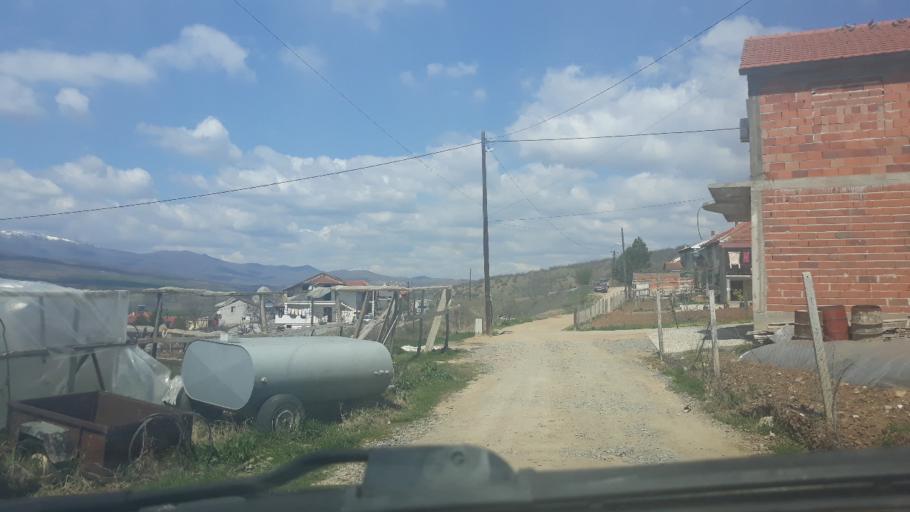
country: MK
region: Caska
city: Caska
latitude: 41.6501
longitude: 21.6948
